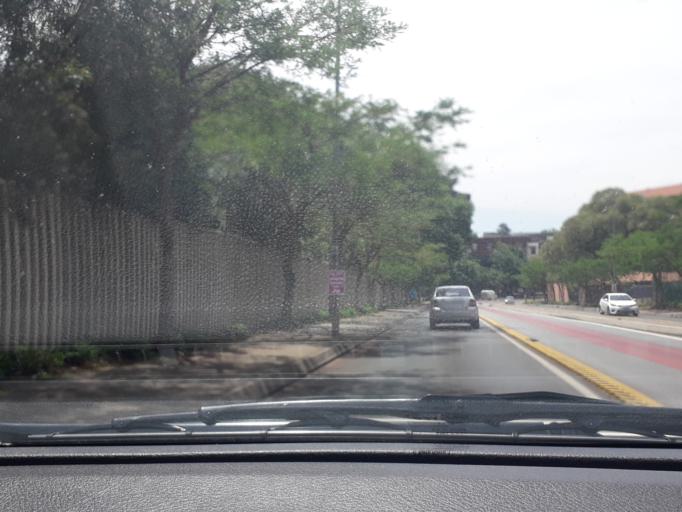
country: ZA
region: Gauteng
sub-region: City of Johannesburg Metropolitan Municipality
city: Johannesburg
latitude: -26.1869
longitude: 28.0359
